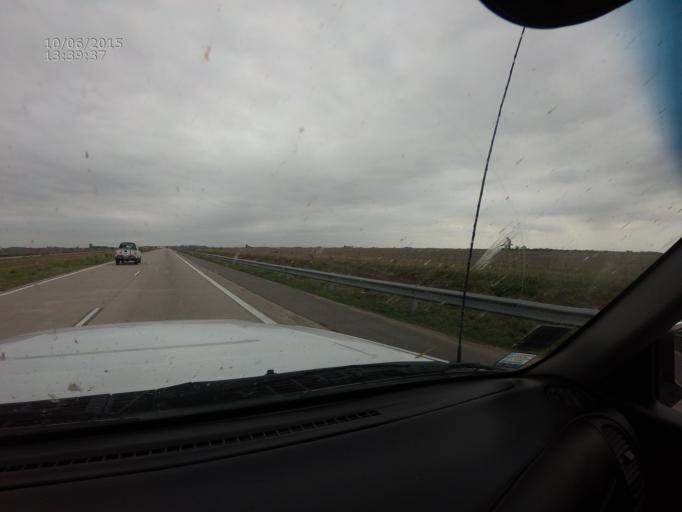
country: AR
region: Cordoba
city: Leones
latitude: -32.5995
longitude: -62.4606
